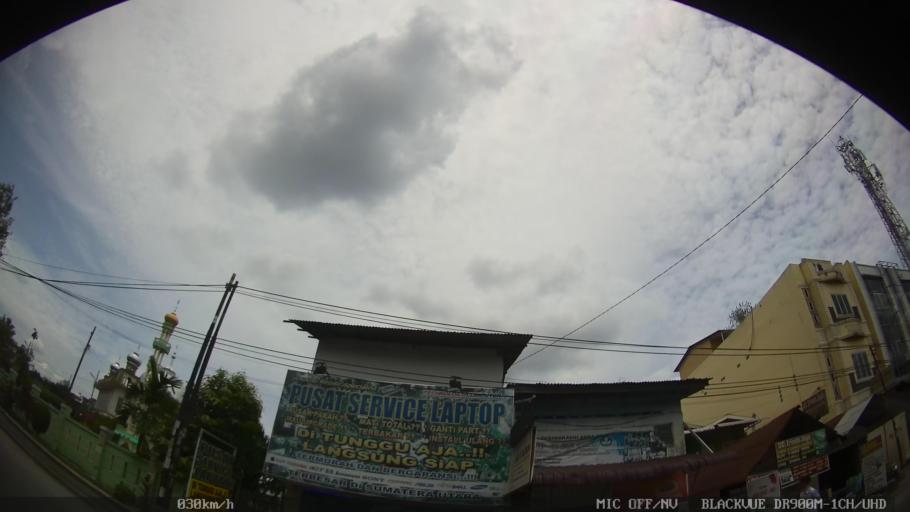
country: ID
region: North Sumatra
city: Medan
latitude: 3.5631
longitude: 98.6624
